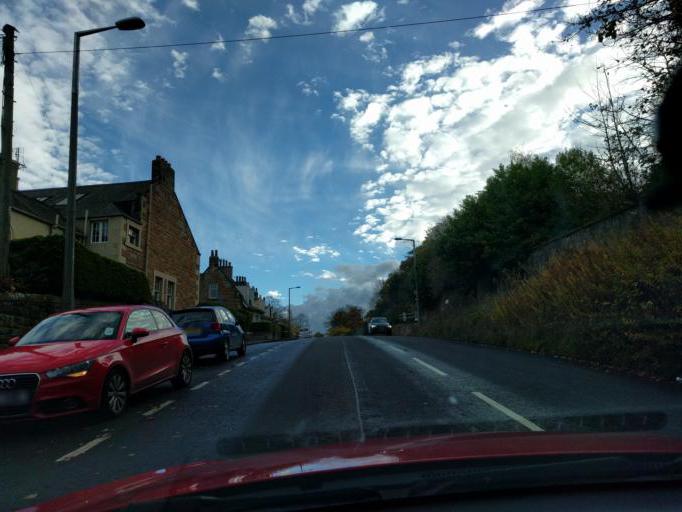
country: GB
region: Scotland
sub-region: Edinburgh
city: Colinton
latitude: 55.9238
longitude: -3.2243
